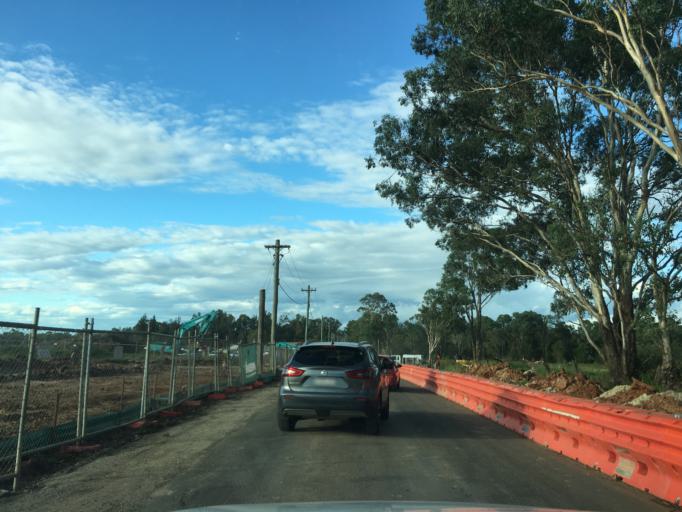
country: AU
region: New South Wales
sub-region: Campbelltown Municipality
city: Denham Court
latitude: -33.9675
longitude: 150.8014
